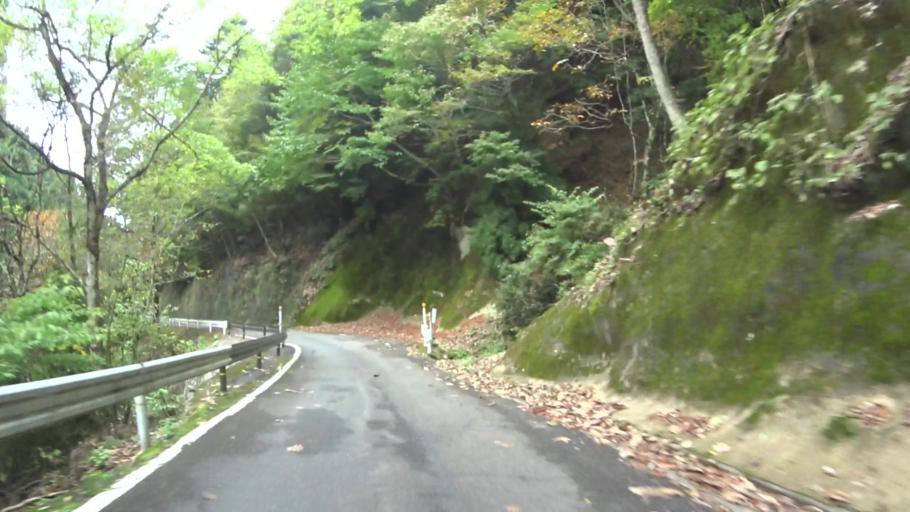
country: JP
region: Fukui
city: Obama
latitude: 35.2744
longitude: 135.7144
